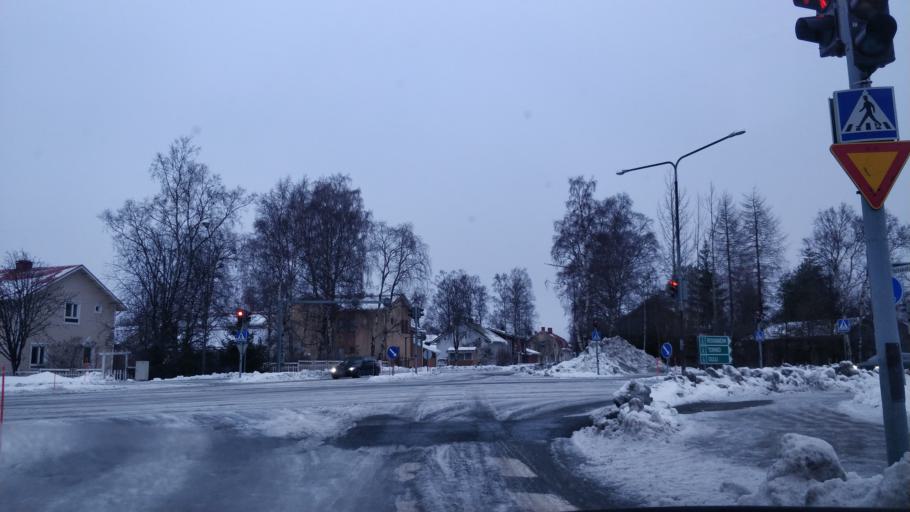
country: FI
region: Lapland
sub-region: Kemi-Tornio
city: Kemi
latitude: 65.7391
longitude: 24.5614
